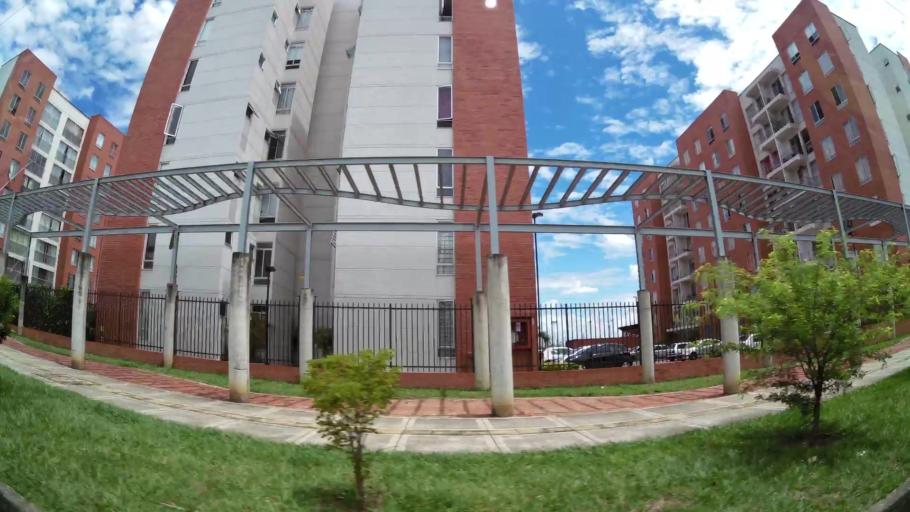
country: CO
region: Valle del Cauca
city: Cali
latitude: 3.3743
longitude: -76.5162
